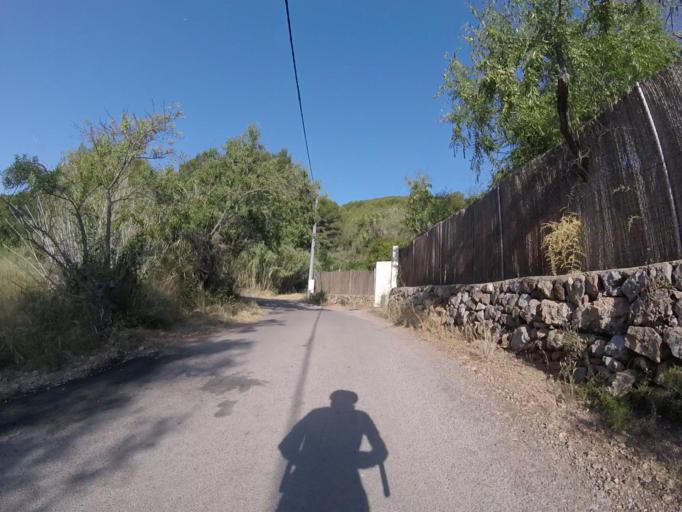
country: ES
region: Valencia
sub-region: Provincia de Castello
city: Benicassim
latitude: 40.0875
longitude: 0.0549
